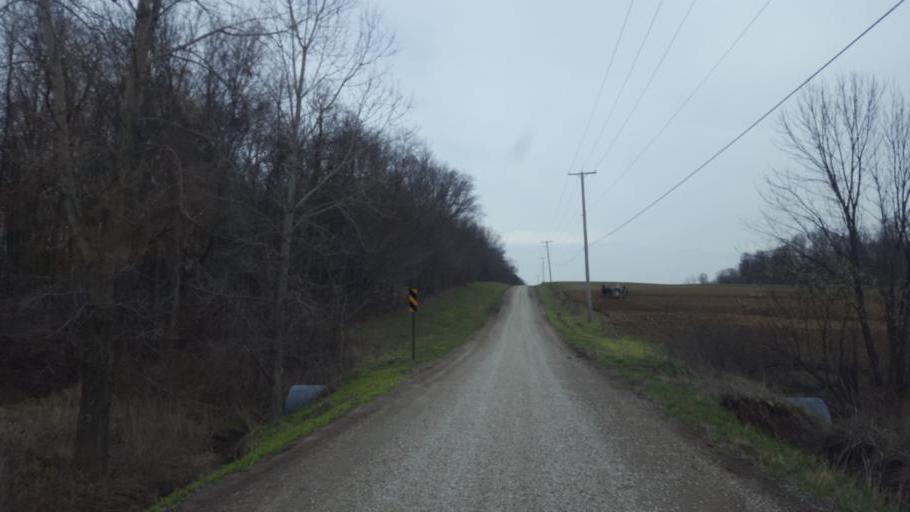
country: US
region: Ohio
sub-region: Richland County
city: Lexington
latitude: 40.5864
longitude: -82.6290
